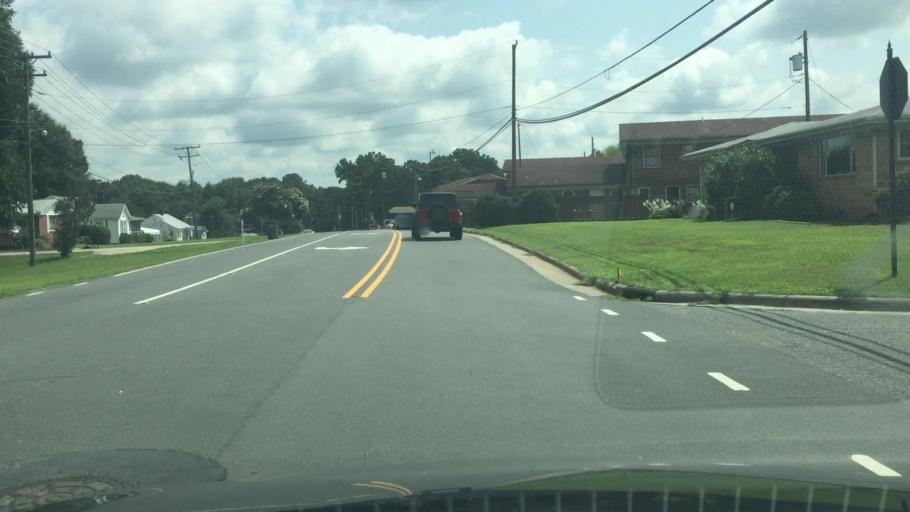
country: US
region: North Carolina
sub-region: Cabarrus County
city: Kannapolis
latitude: 35.4748
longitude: -80.6400
